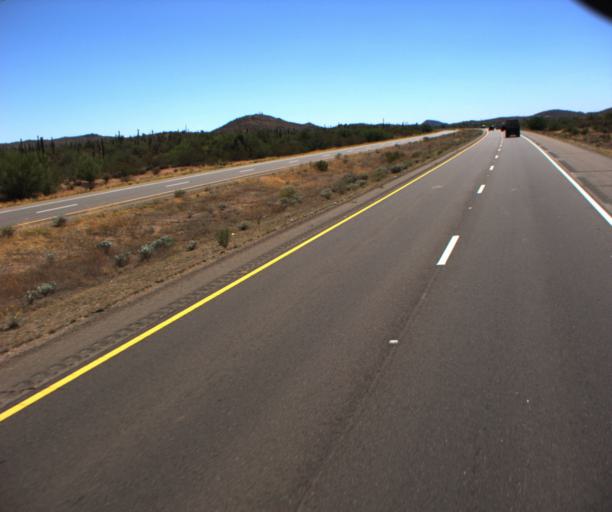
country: US
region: Arizona
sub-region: Maricopa County
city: Fountain Hills
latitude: 33.5772
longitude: -111.6884
